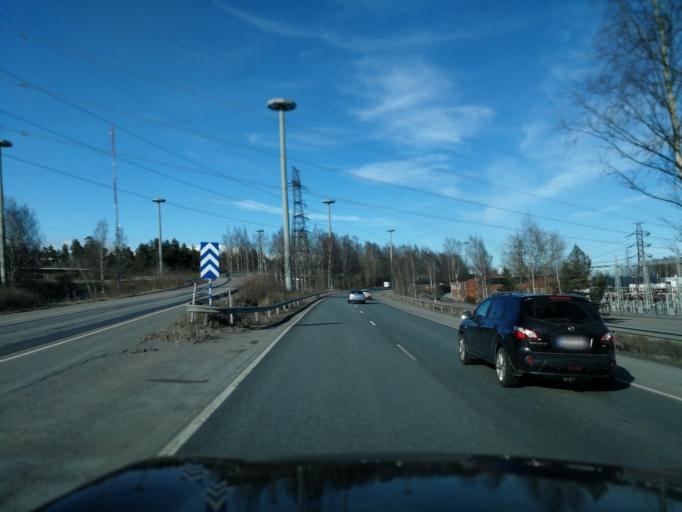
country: FI
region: Uusimaa
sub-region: Helsinki
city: Vantaa
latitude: 60.2059
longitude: 25.0468
